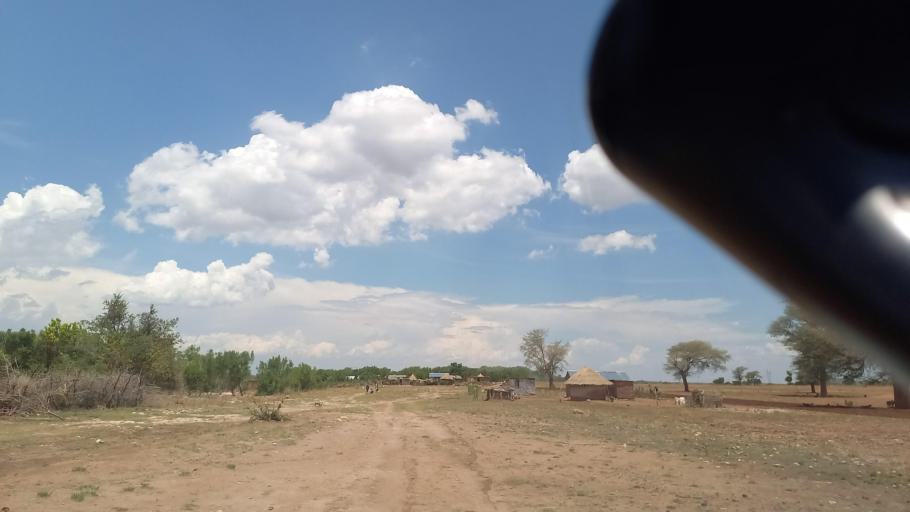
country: ZM
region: Southern
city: Mazabuka
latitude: -16.1098
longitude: 27.8235
